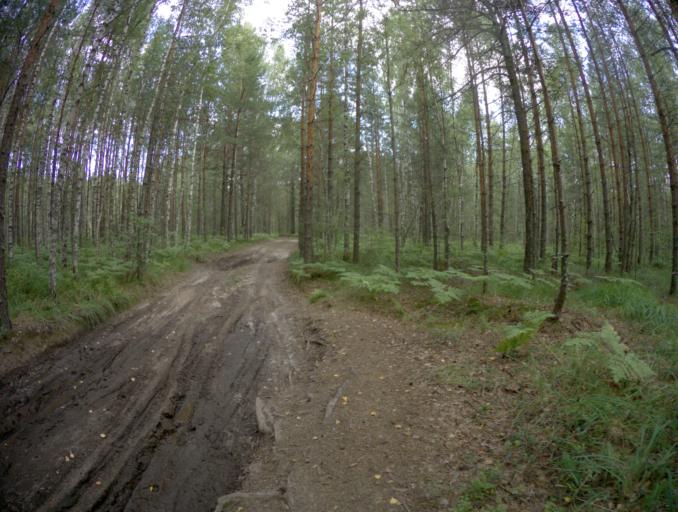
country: RU
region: Vladimir
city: Vorsha
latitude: 55.9496
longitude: 40.1942
